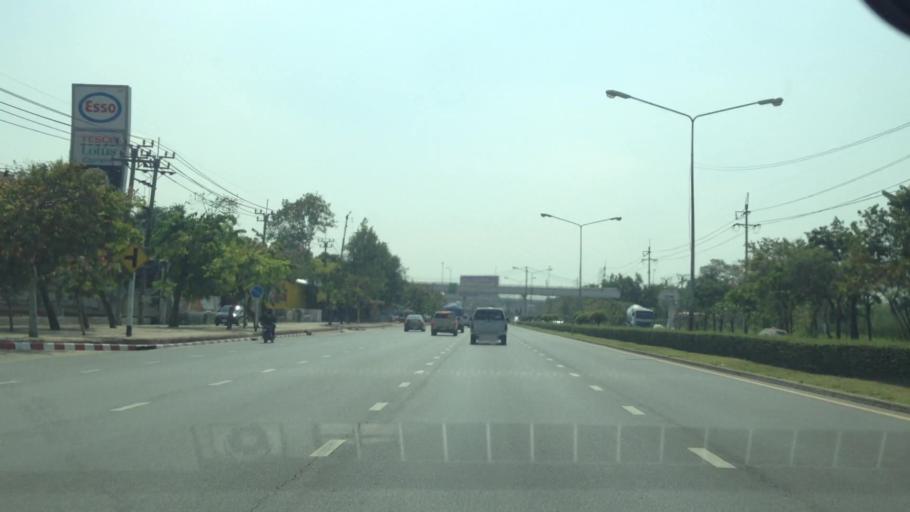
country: TH
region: Bangkok
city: Sai Mai
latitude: 13.9320
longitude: 100.6258
